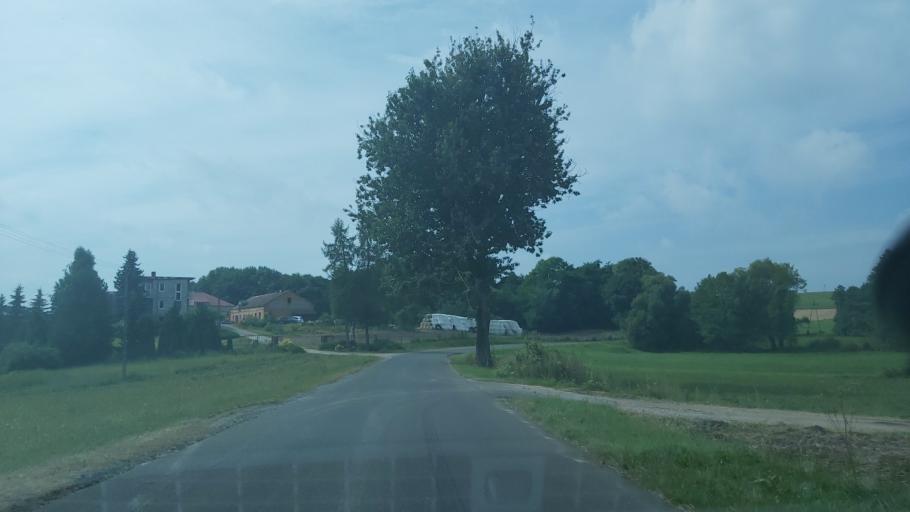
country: PL
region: Kujawsko-Pomorskie
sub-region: Powiat golubsko-dobrzynski
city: Zbojno
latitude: 53.0473
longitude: 19.1462
